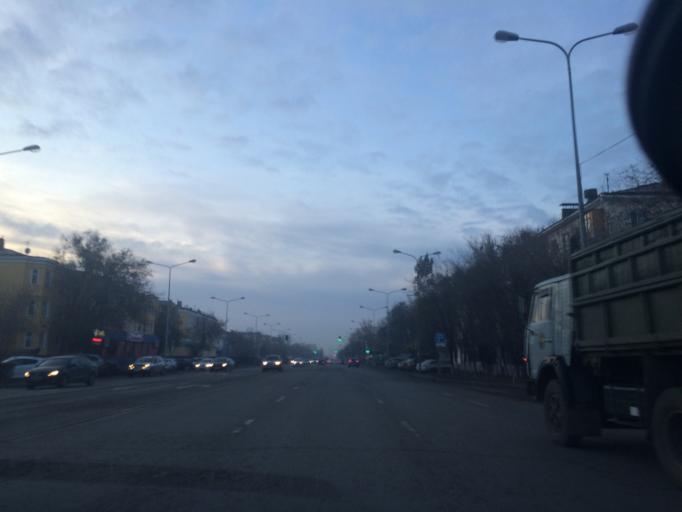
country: KZ
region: Astana Qalasy
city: Astana
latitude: 51.1847
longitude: 71.4085
